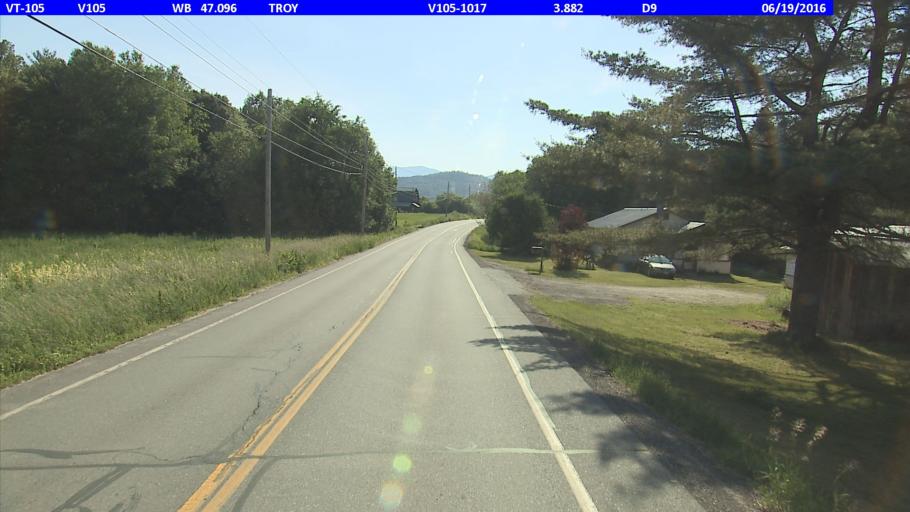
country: US
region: Vermont
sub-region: Orleans County
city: Newport
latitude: 44.9919
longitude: -72.3802
